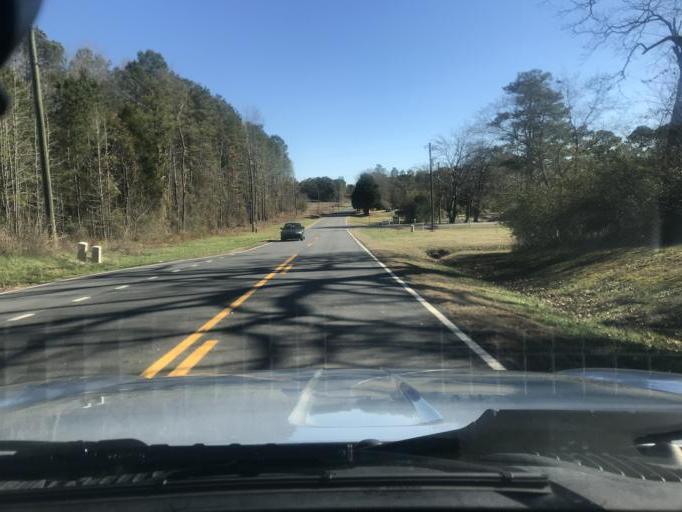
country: US
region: Georgia
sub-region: Barrow County
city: Russell
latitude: 33.9108
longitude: -83.7523
